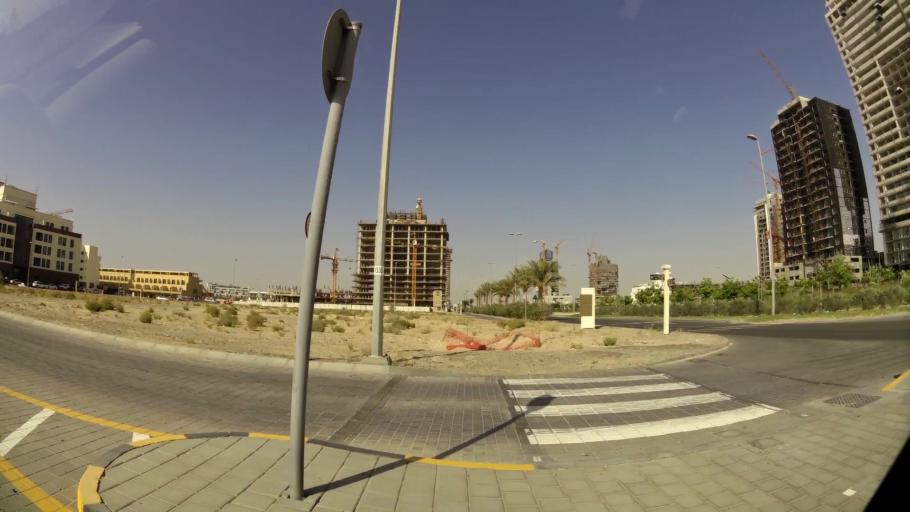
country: AE
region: Dubai
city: Dubai
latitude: 25.0542
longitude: 55.1983
